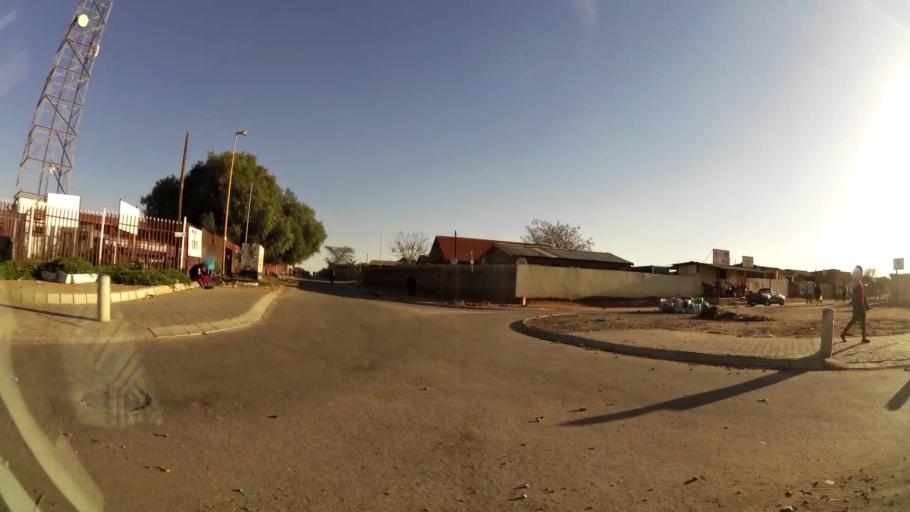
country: ZA
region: Gauteng
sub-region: Ekurhuleni Metropolitan Municipality
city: Tembisa
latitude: -26.0066
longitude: 28.2270
